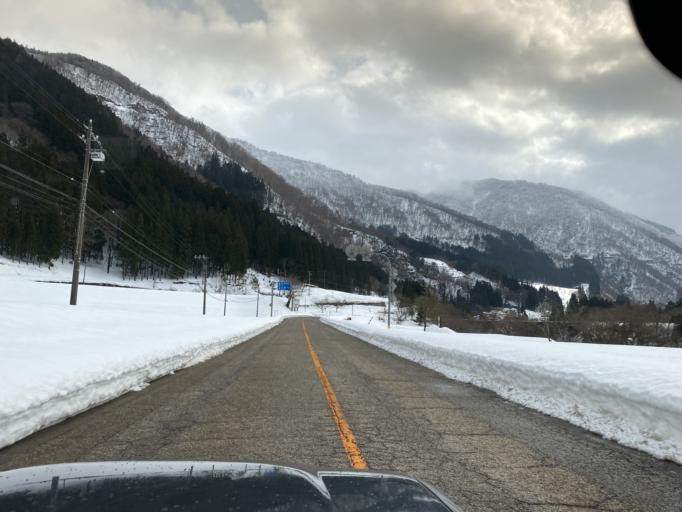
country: JP
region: Toyama
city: Fukumitsu
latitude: 36.3691
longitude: 136.8706
